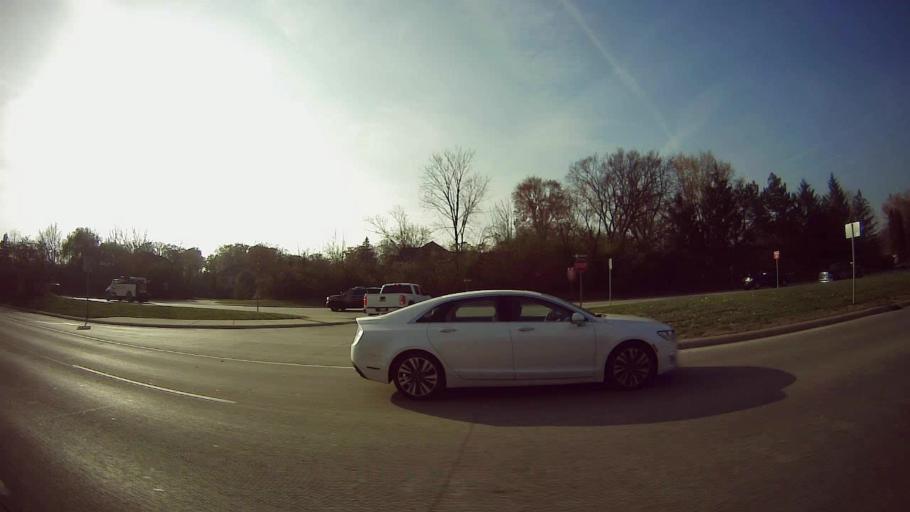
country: US
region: Michigan
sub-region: Oakland County
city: Bingham Farms
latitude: 42.5097
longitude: -83.2853
